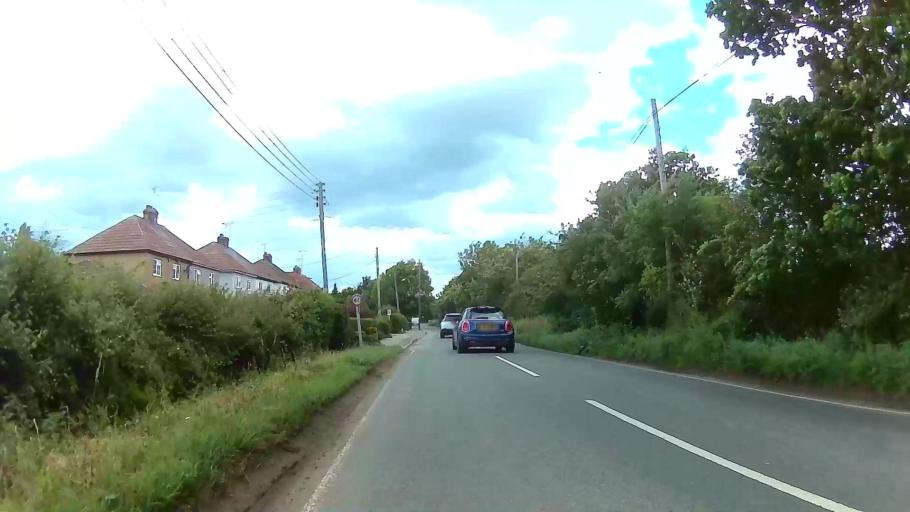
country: GB
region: England
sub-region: Greater London
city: Collier Row
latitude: 51.6336
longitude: 0.1444
